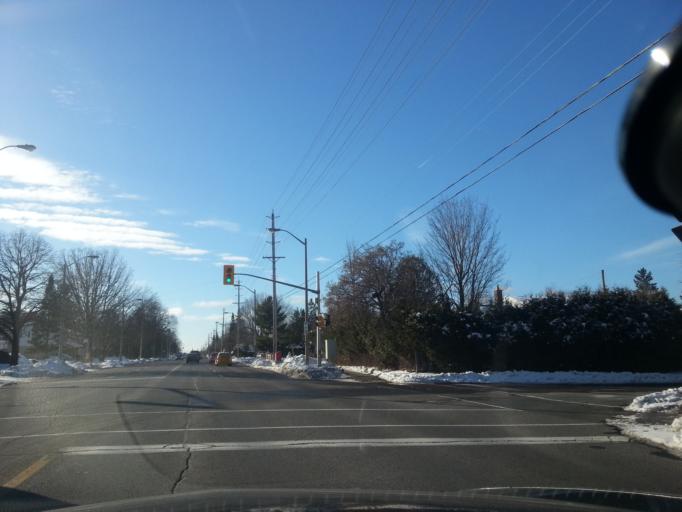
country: CA
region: Ontario
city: Ottawa
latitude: 45.3667
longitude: -75.6724
